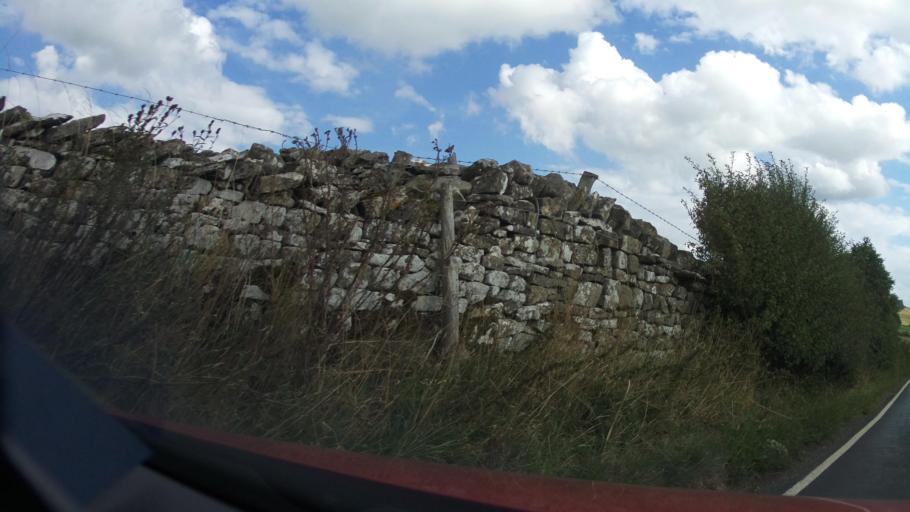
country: GB
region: England
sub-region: North Yorkshire
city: Leyburn
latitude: 54.3670
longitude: -1.8256
